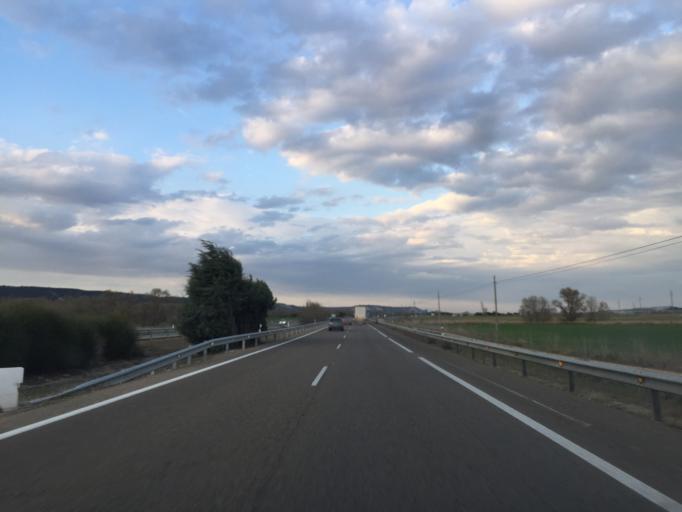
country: ES
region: Castille and Leon
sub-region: Provincia de Palencia
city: Cordovilla la Real
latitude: 42.0590
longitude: -4.2351
